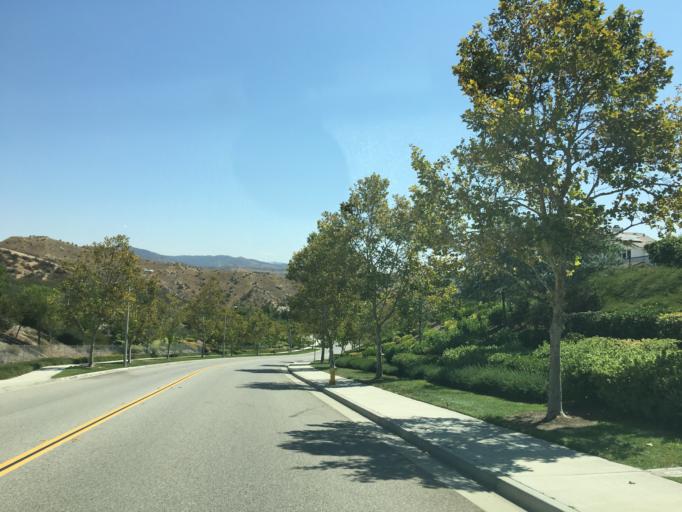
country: US
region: California
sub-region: Los Angeles County
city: Valencia
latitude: 34.4733
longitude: -118.5598
